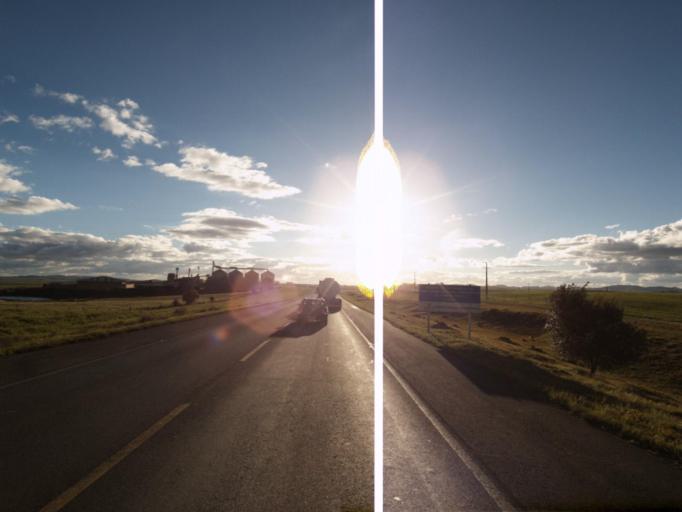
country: BR
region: Santa Catarina
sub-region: Campos Novos
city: Campos Novos
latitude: -27.3685
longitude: -51.2555
